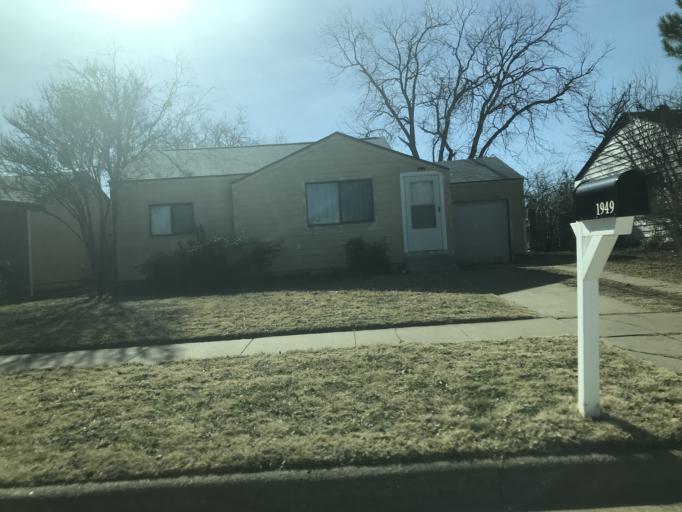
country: US
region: Texas
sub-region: Taylor County
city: Abilene
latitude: 32.4775
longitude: -99.7439
